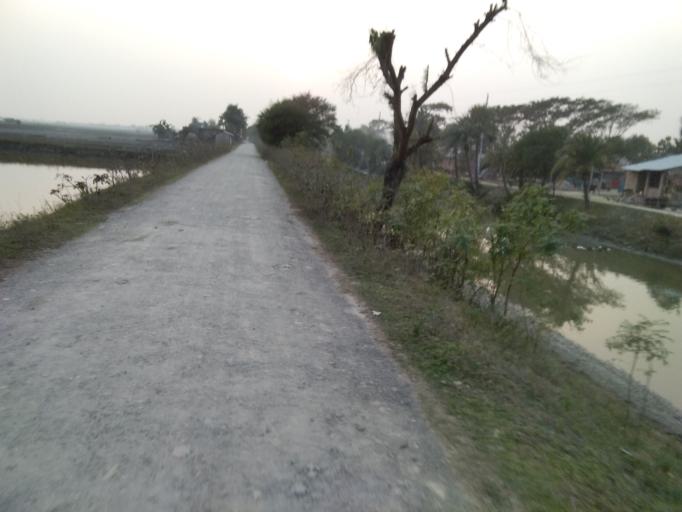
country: BD
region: Khulna
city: Satkhira
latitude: 22.6551
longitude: 89.0250
